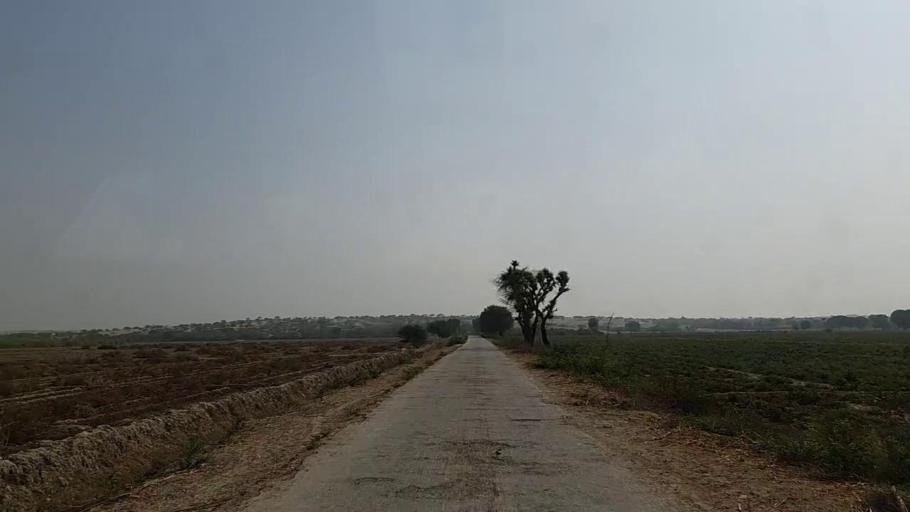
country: PK
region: Sindh
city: Naukot
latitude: 24.7510
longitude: 69.3472
